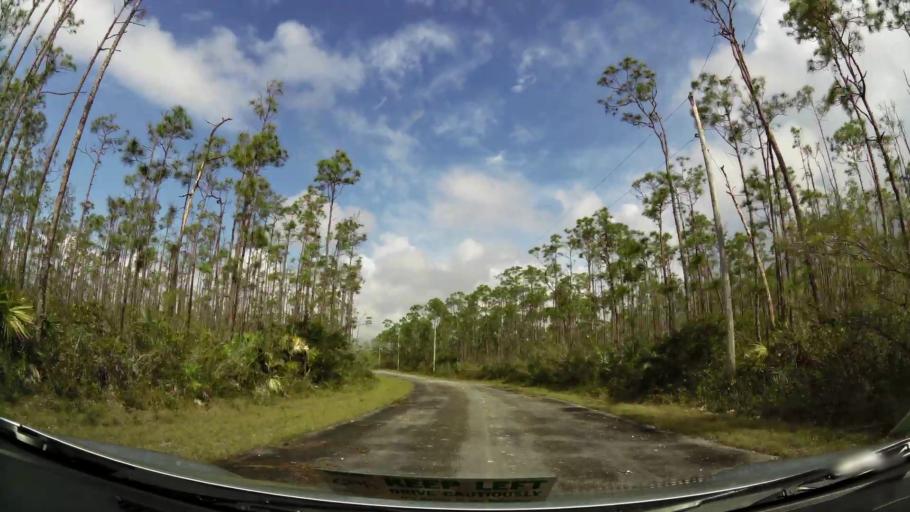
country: BS
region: Freeport
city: Lucaya
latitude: 26.5788
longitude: -78.5518
